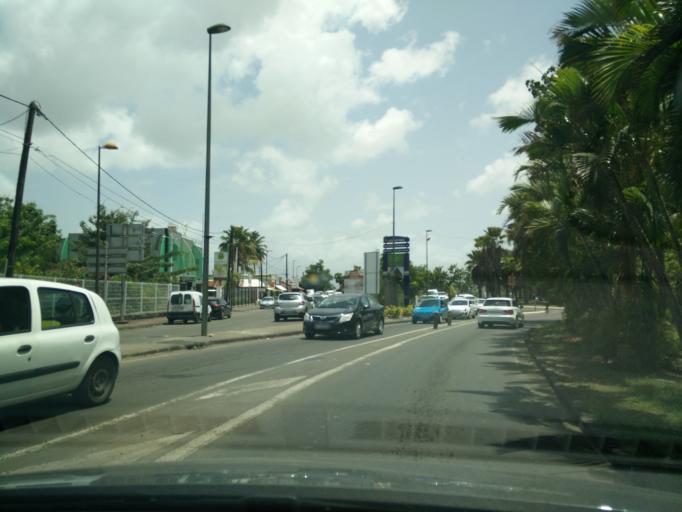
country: GP
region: Guadeloupe
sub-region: Guadeloupe
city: Les Abymes
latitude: 16.2660
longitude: -61.5099
